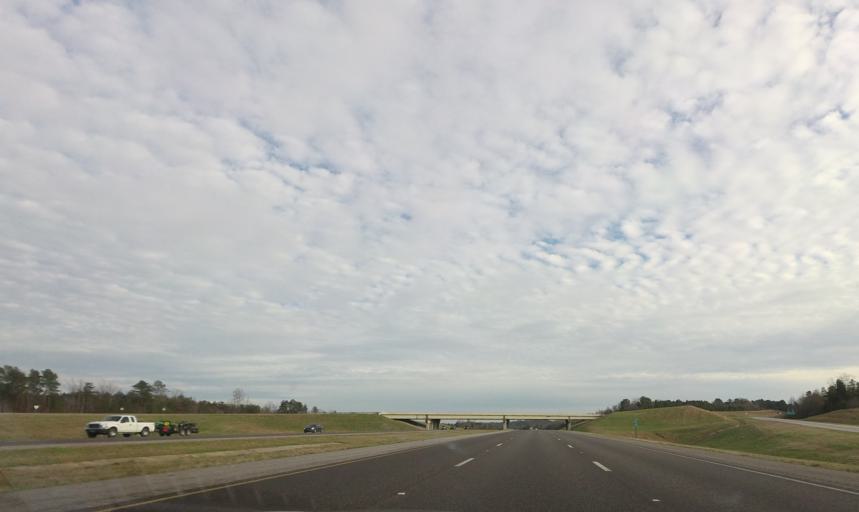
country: US
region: Alabama
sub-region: Jefferson County
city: Adamsville
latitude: 33.6122
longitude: -86.9314
